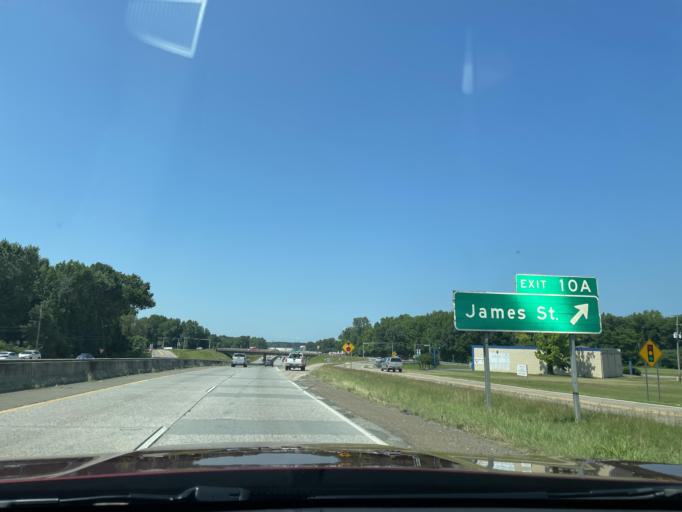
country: US
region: Arkansas
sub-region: Pulaski County
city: Jacksonville
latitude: 34.8771
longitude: -92.1163
